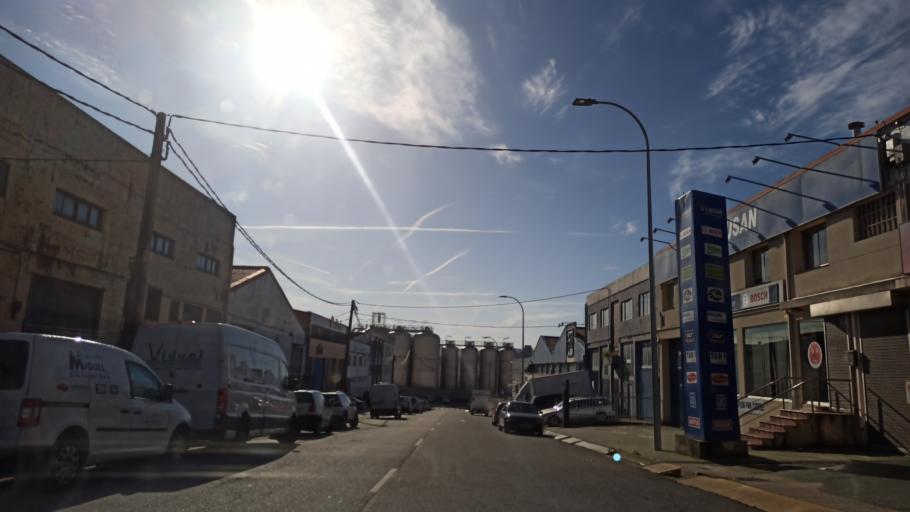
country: ES
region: Galicia
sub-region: Provincia da Coruna
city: A Coruna
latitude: 43.3556
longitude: -8.4205
